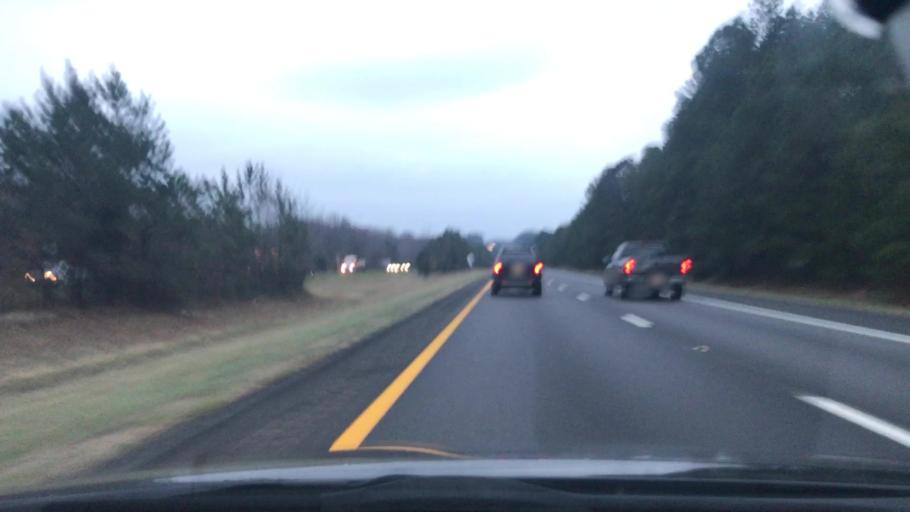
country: US
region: Tennessee
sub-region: Sumner County
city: White House
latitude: 36.4481
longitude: -86.6981
